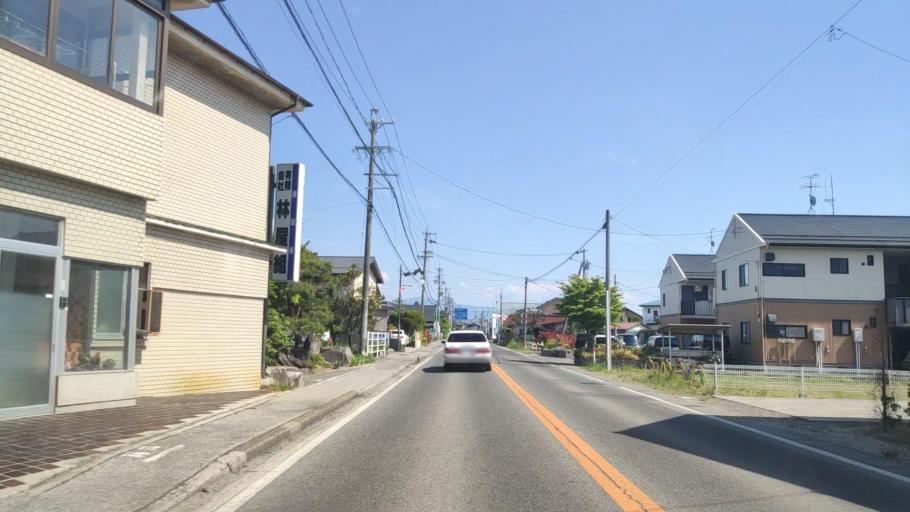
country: JP
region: Nagano
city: Hotaka
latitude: 36.3472
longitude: 137.8843
